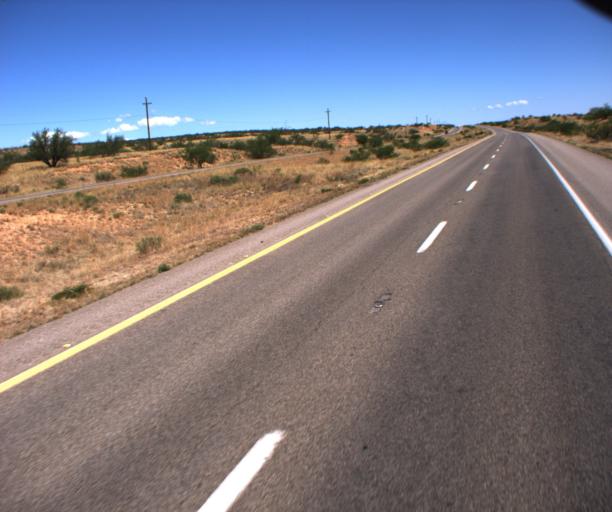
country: US
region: Arizona
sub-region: Cochise County
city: Whetstone
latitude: 31.8469
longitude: -110.3413
